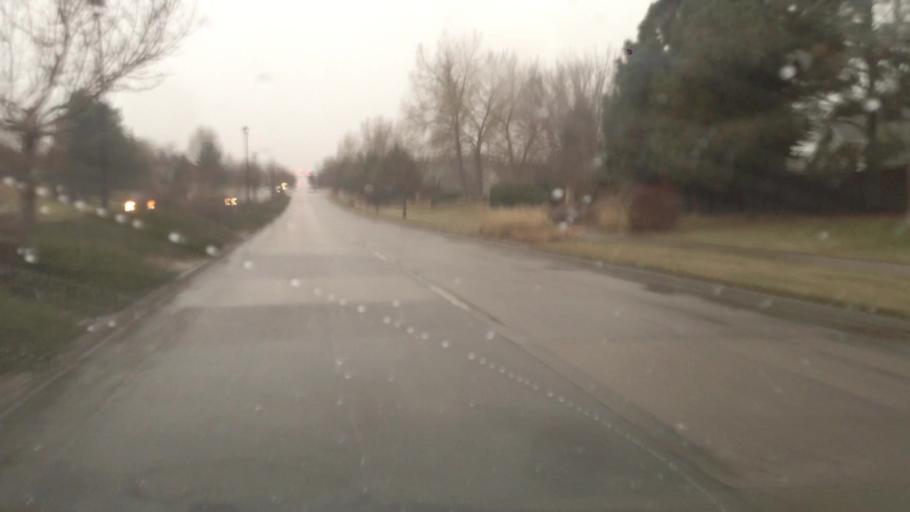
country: US
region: Colorado
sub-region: Douglas County
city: Stonegate
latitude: 39.5217
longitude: -104.7935
